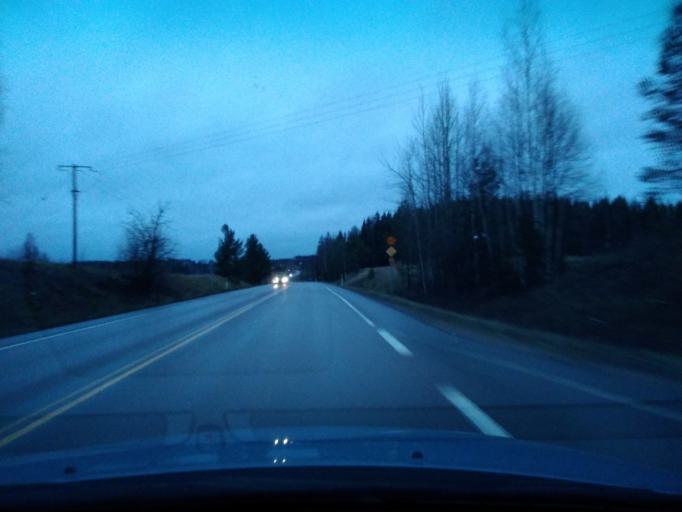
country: FI
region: Uusimaa
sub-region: Porvoo
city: Askola
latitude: 60.4494
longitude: 25.5852
